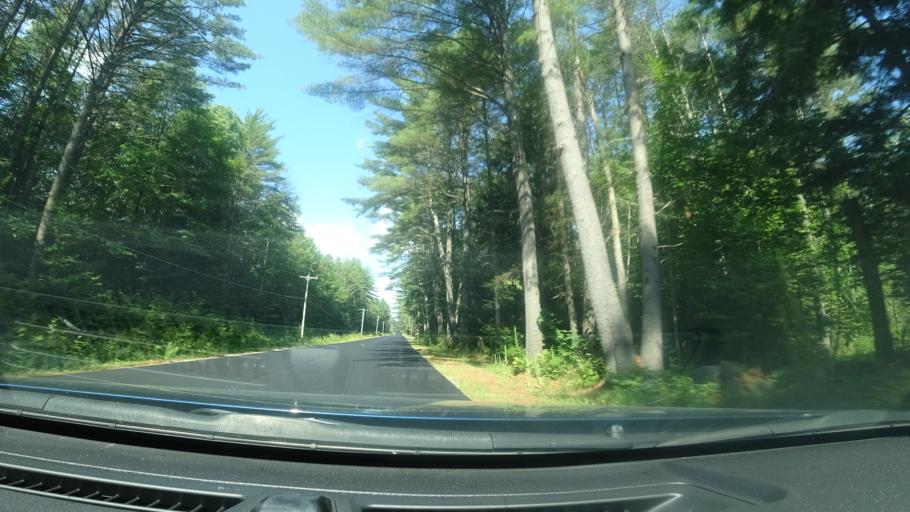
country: US
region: New York
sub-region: Warren County
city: Warrensburg
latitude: 43.6519
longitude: -73.8184
